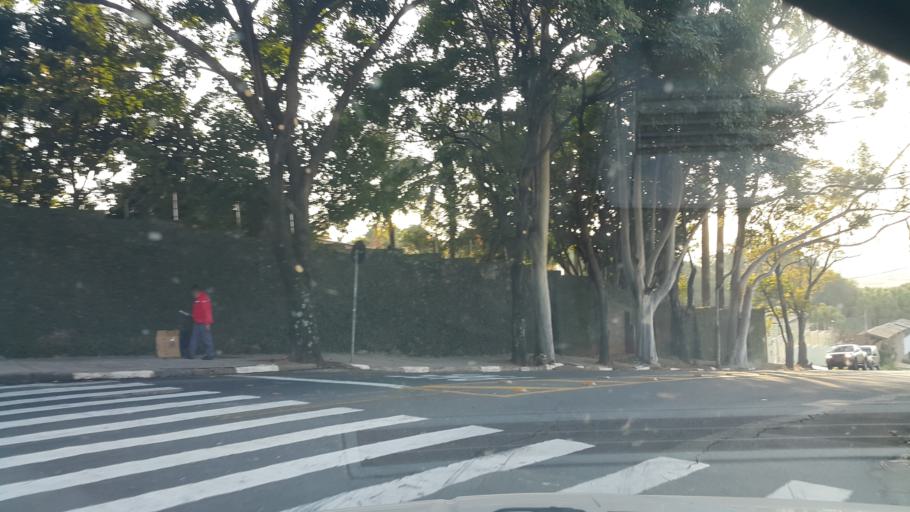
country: BR
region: Sao Paulo
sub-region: Campinas
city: Campinas
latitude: -22.8656
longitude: -47.0549
